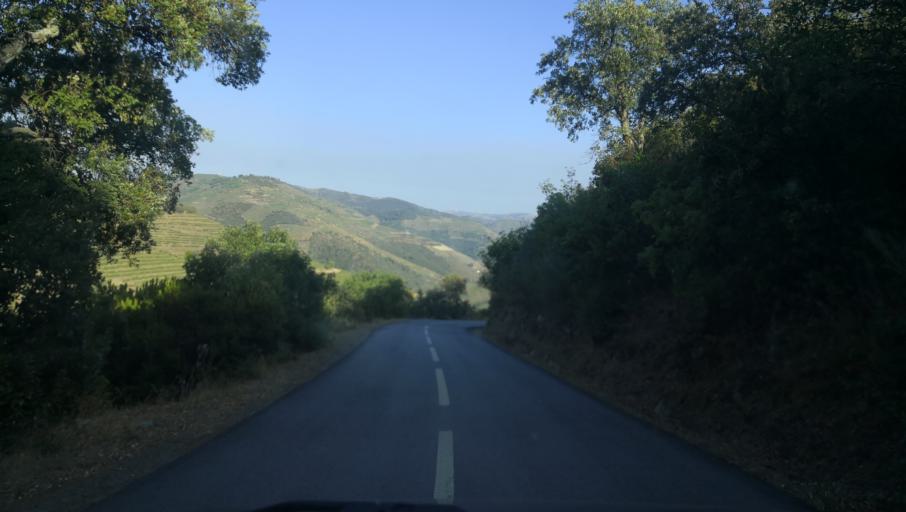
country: PT
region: Vila Real
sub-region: Sabrosa
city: Vilela
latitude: 41.1660
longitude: -7.6014
